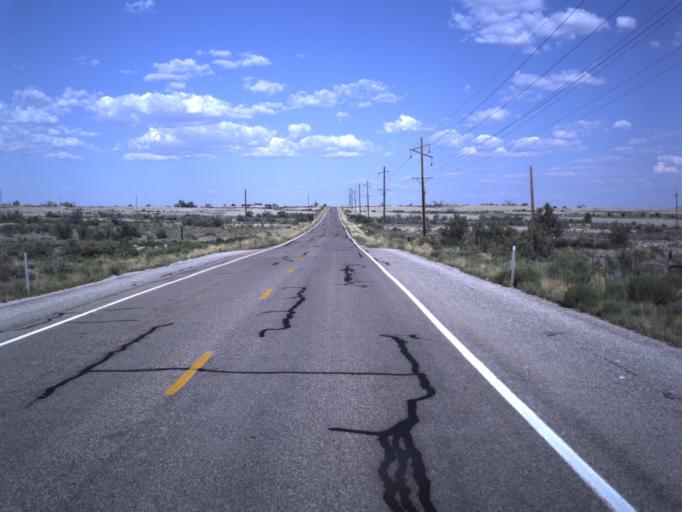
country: US
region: Utah
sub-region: Emery County
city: Huntington
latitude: 39.3450
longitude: -110.9266
